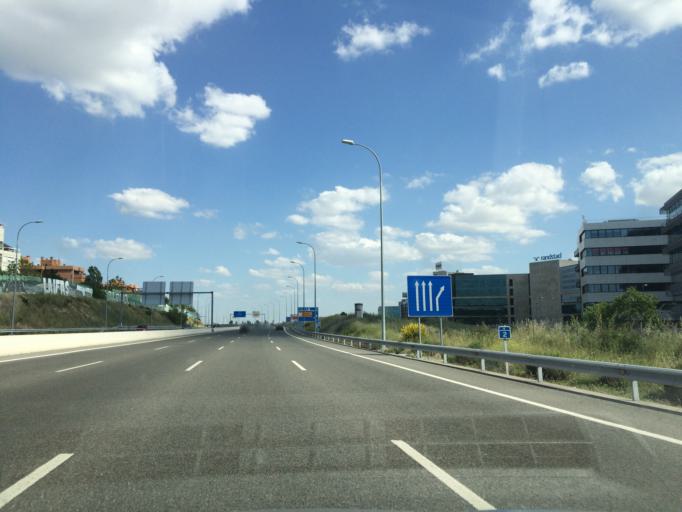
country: ES
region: Madrid
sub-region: Provincia de Madrid
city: Hortaleza
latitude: 40.4775
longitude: -3.6330
